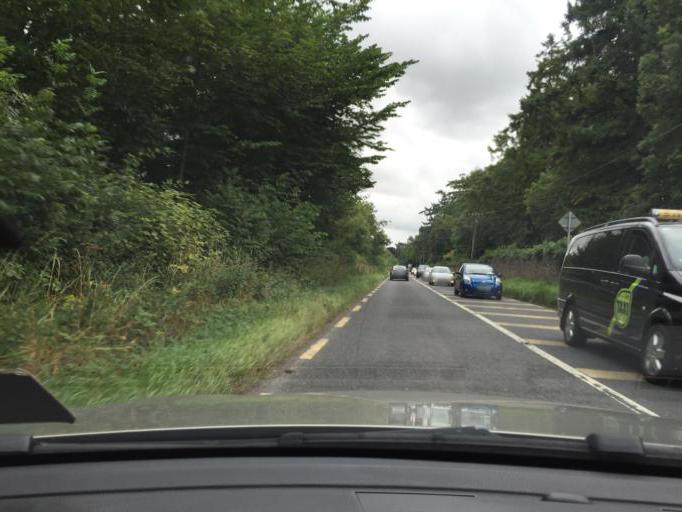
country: IE
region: Leinster
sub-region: Kildare
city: Maynooth
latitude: 53.3975
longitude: -6.5559
